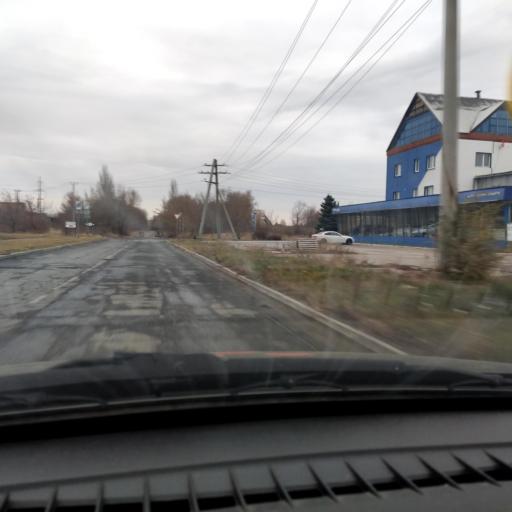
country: RU
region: Samara
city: Tol'yatti
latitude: 53.5535
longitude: 49.3235
